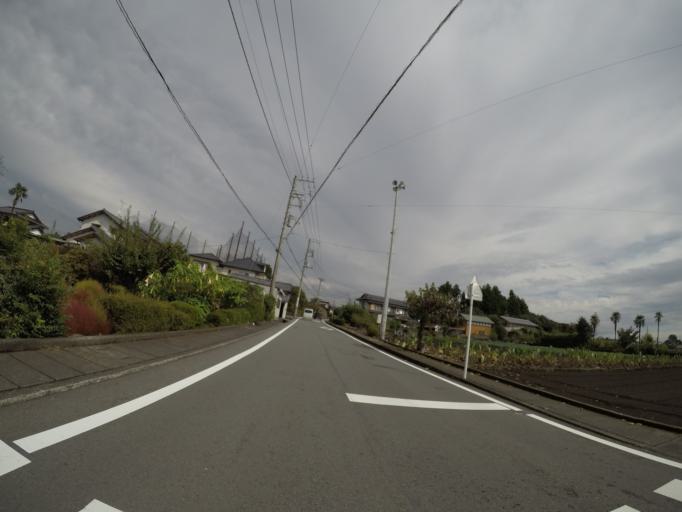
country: JP
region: Shizuoka
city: Fuji
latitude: 35.2053
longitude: 138.6680
